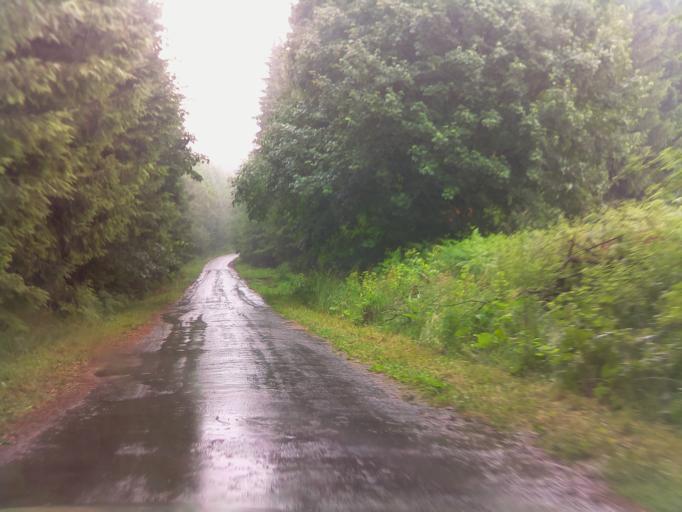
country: BE
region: Wallonia
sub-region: Province de Namur
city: Bievre
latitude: 49.9560
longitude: 5.0060
